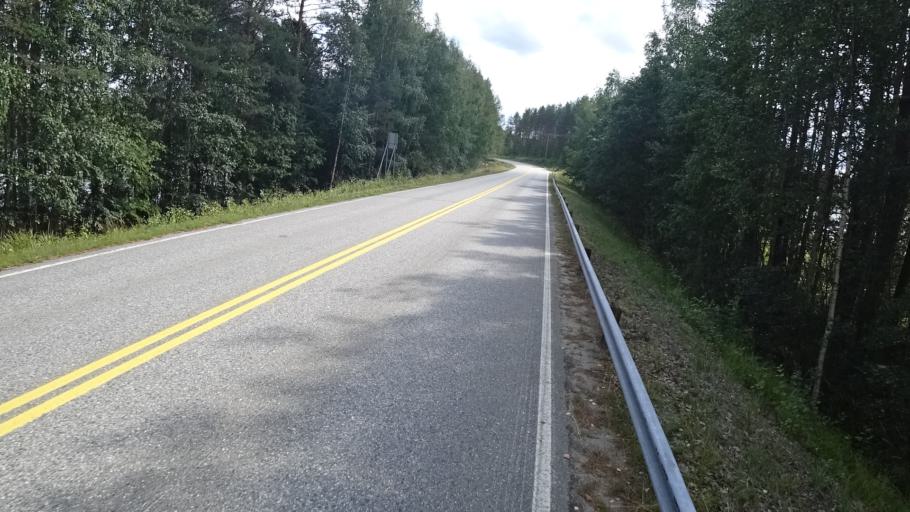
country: FI
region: North Karelia
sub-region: Joensuu
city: Ilomantsi
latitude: 62.6192
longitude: 31.2021
